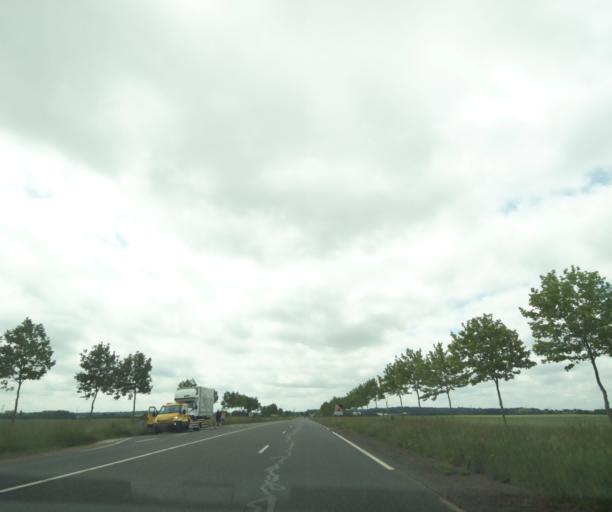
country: FR
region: Poitou-Charentes
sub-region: Departement des Deux-Sevres
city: Saint-Varent
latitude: 46.8435
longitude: -0.2086
